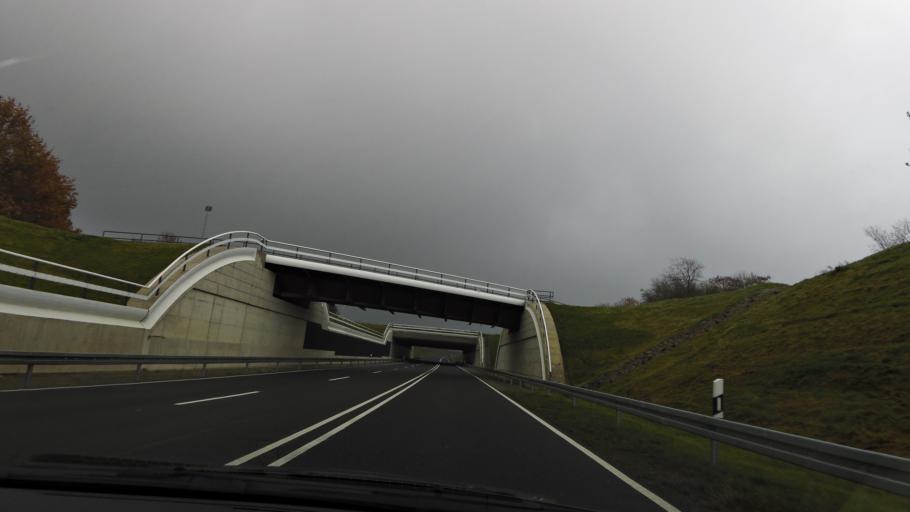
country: DE
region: North Rhine-Westphalia
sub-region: Regierungsbezirk Koln
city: Gangelt
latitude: 51.0127
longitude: 6.0400
